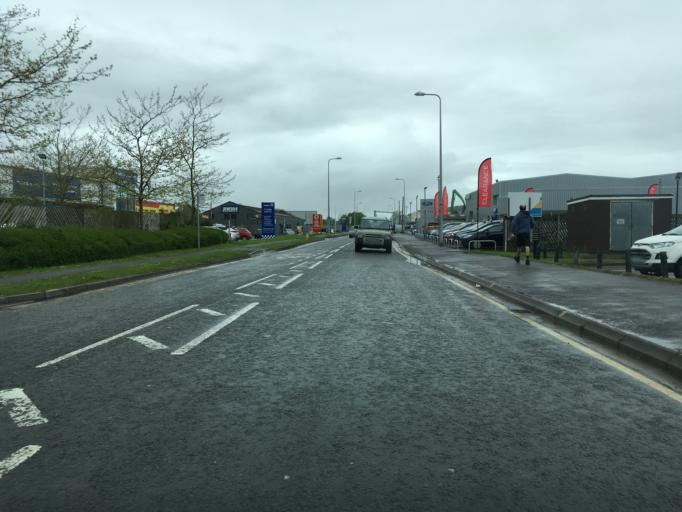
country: GB
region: England
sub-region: North Somerset
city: Weston-super-Mare
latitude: 51.3401
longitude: -2.9603
